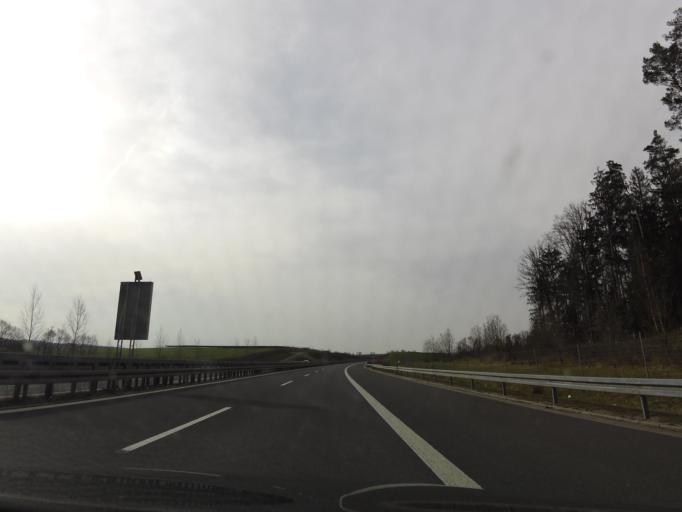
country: DE
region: Bavaria
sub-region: Upper Franconia
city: Rodental
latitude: 50.2396
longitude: 11.0478
